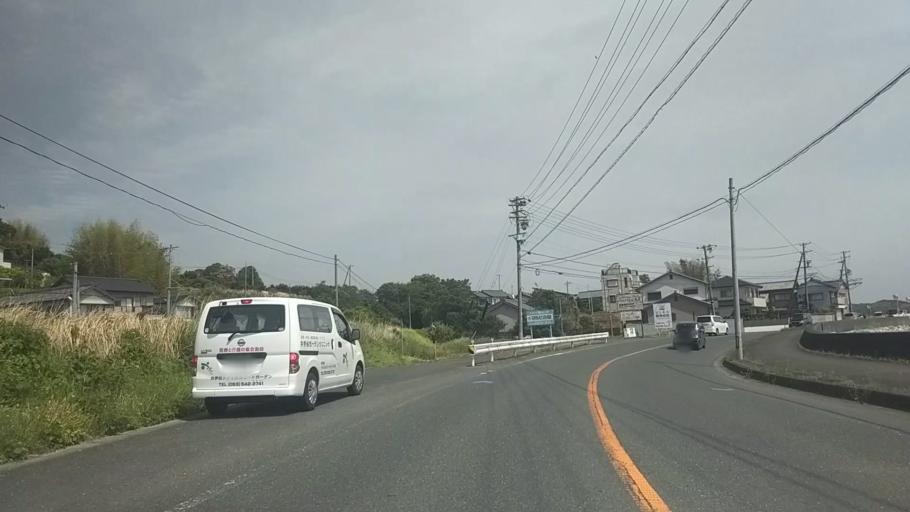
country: JP
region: Shizuoka
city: Kosai-shi
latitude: 34.8021
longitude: 137.6254
